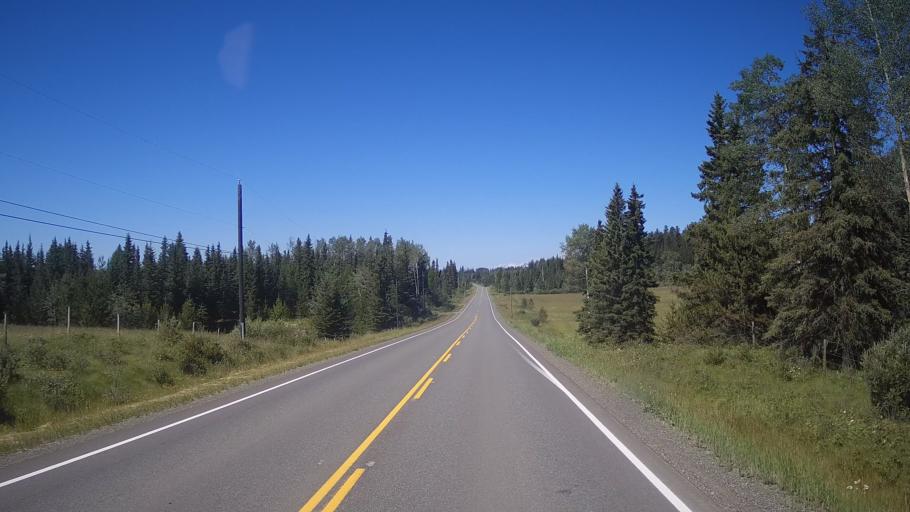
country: CA
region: British Columbia
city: Cache Creek
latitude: 51.5443
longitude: -120.9500
